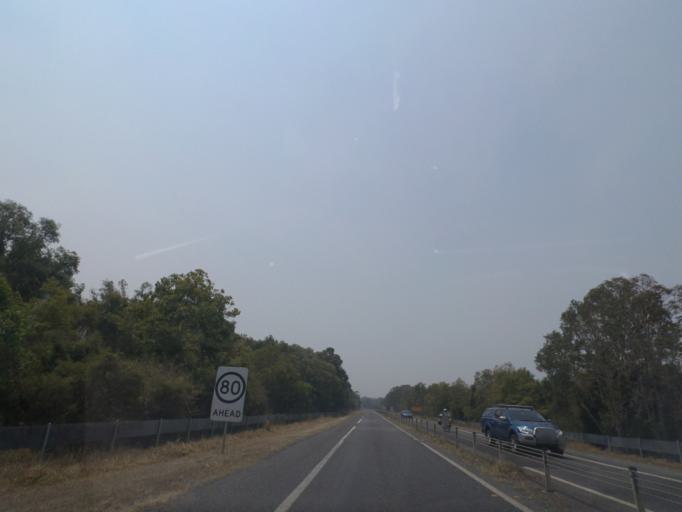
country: AU
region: New South Wales
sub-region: Ballina
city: Ballina
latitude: -28.9332
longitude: 153.4730
